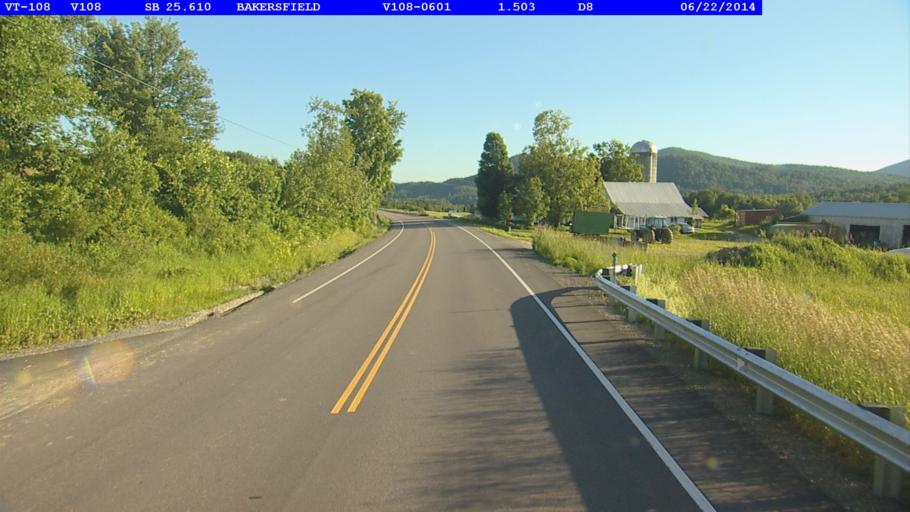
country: US
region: Vermont
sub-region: Franklin County
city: Enosburg Falls
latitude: 44.7546
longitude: -72.8216
